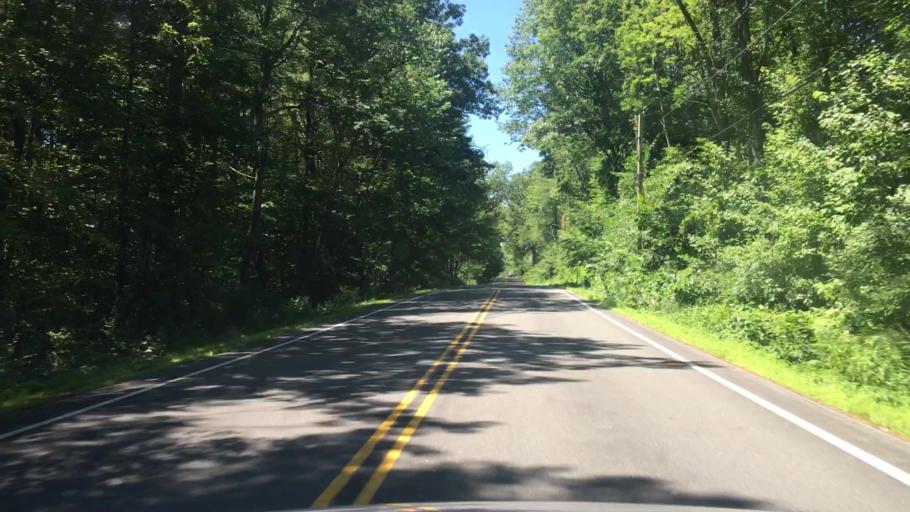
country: US
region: New Hampshire
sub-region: Merrimack County
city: Hopkinton
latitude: 43.1881
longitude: -71.6822
